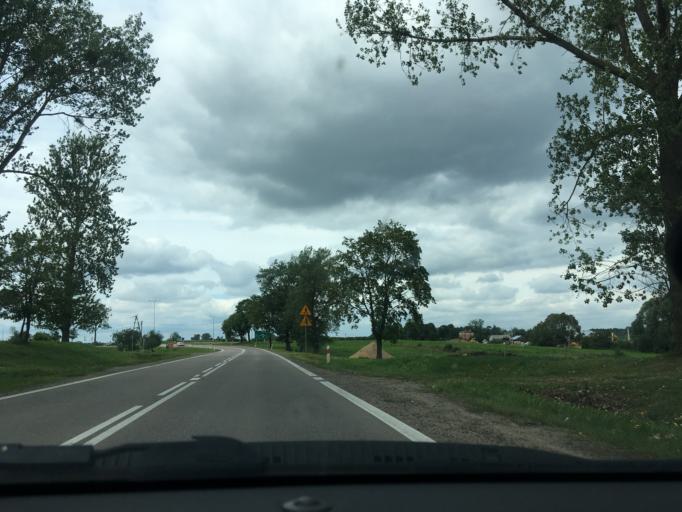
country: PL
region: Podlasie
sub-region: Powiat augustowski
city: Augustow
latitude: 53.8447
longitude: 22.9538
